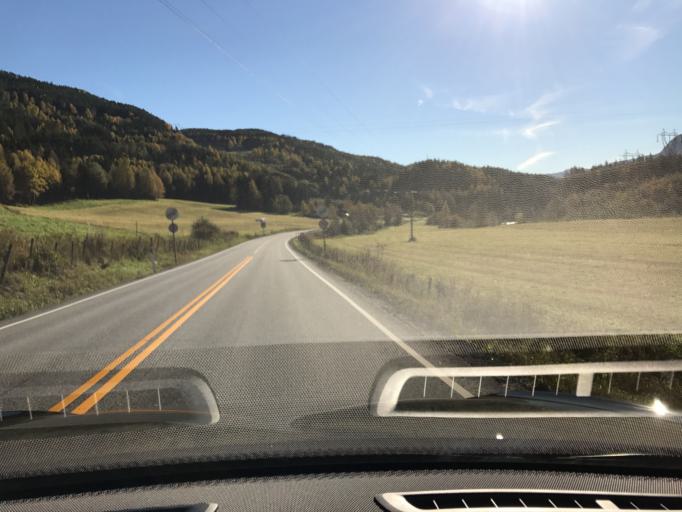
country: NO
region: Buskerud
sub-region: Nes
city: Nesbyen
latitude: 60.6571
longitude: 9.0526
